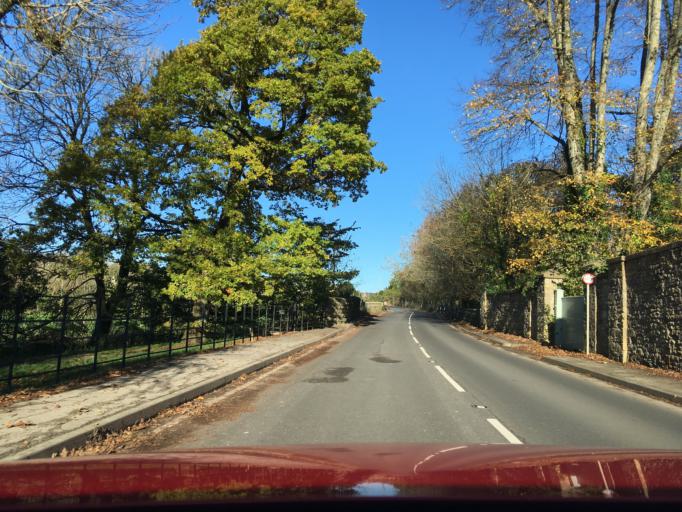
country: GB
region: England
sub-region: Dorset
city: Sherborne
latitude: 50.9471
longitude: -2.5068
